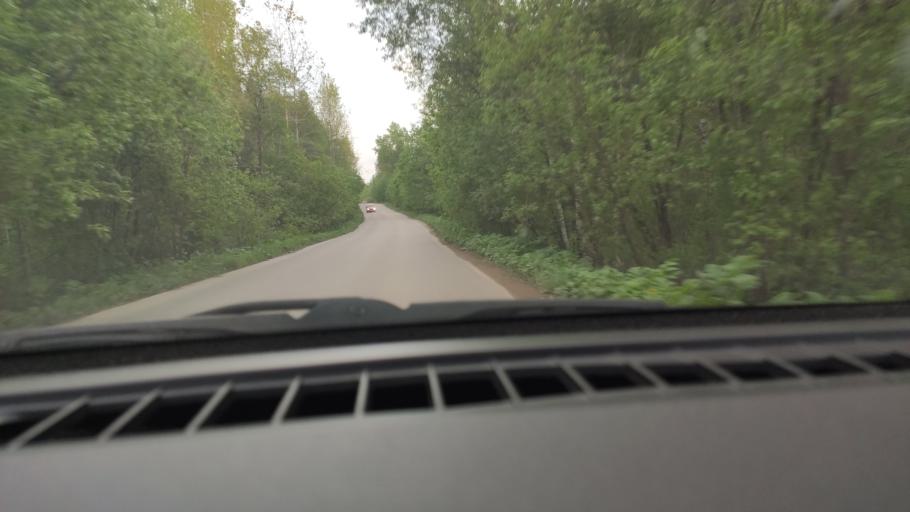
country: RU
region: Perm
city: Overyata
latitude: 58.0760
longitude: 56.0018
